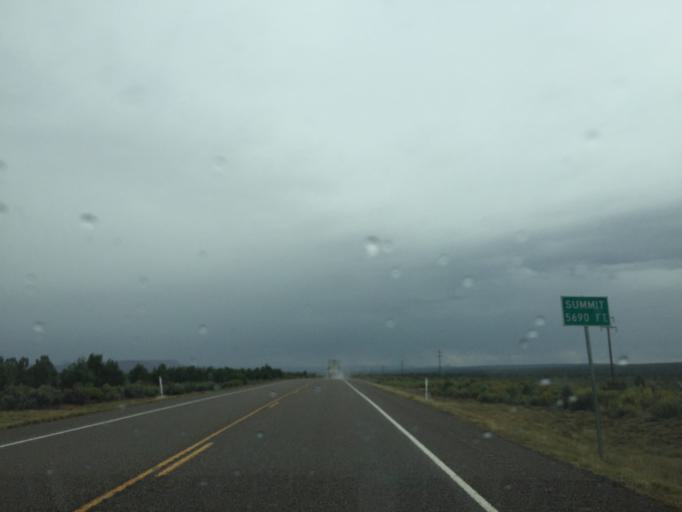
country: US
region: Utah
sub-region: Kane County
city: Kanab
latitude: 37.0723
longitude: -112.1727
